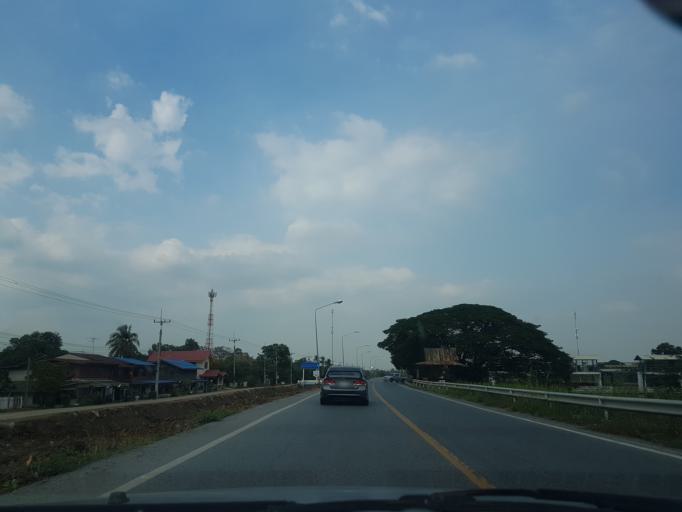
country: TH
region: Sara Buri
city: Nong Saeng
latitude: 14.5040
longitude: 100.7348
